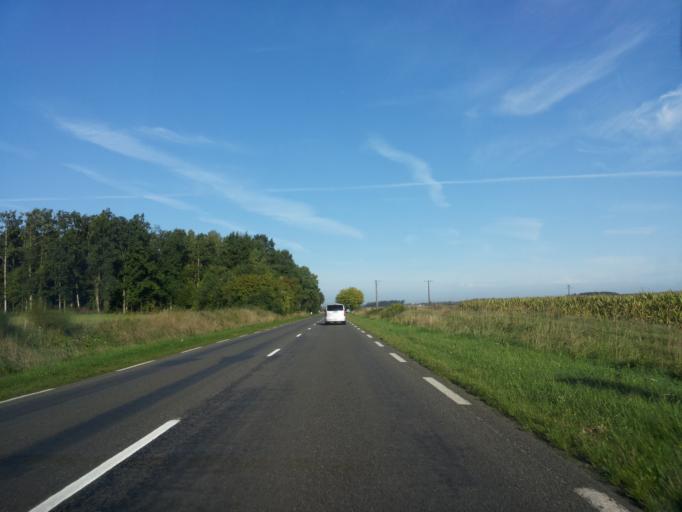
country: FR
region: Picardie
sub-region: Departement de l'Aisne
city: Athies-sous-Laon
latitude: 49.5477
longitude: 3.7255
